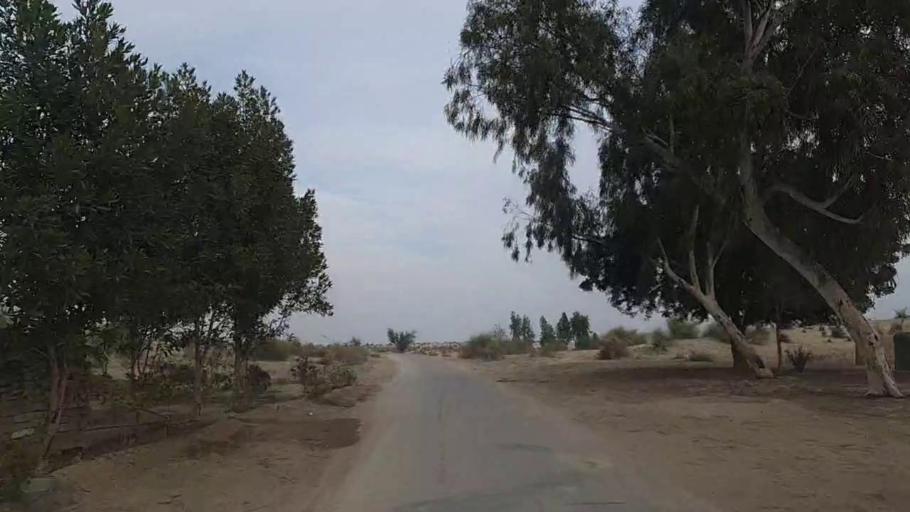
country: PK
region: Sindh
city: Daur
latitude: 26.5103
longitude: 68.4619
